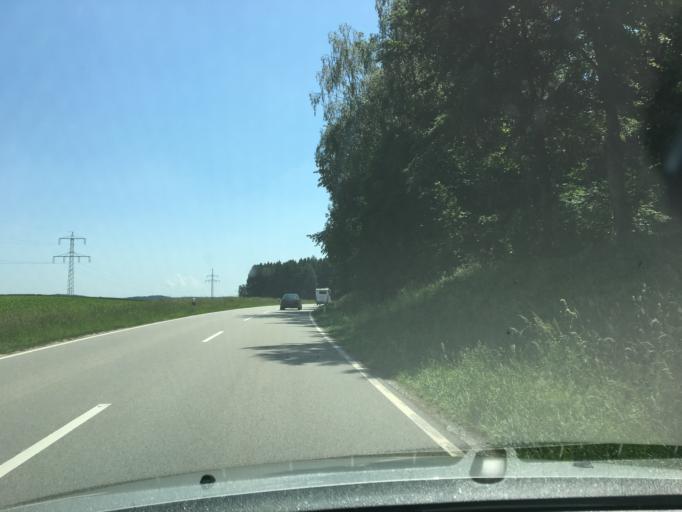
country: DE
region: Bavaria
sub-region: Upper Bavaria
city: Neumarkt-Sankt Veit
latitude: 48.3373
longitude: 12.5193
